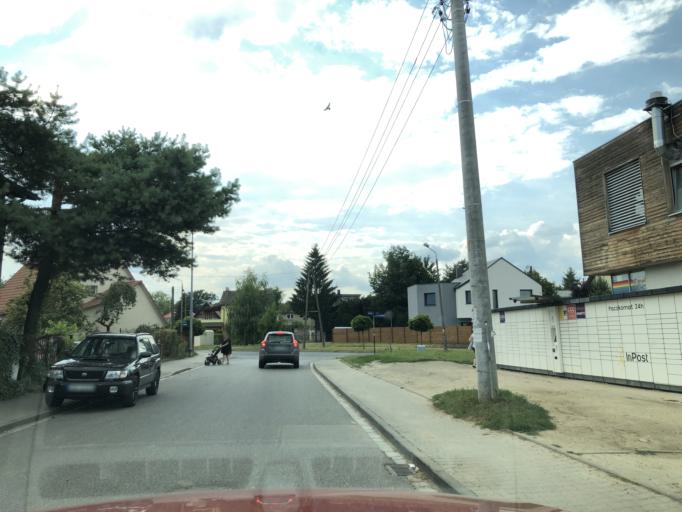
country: PL
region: Lower Silesian Voivodeship
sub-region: Powiat wroclawski
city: Smolec
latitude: 51.1583
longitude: 16.8975
